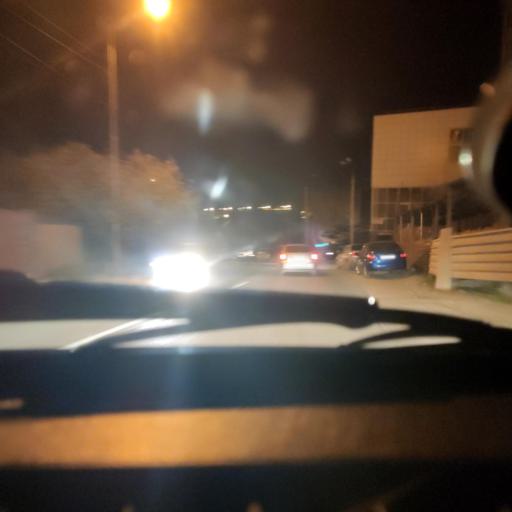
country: RU
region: Bashkortostan
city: Ufa
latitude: 54.7497
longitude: 55.9651
